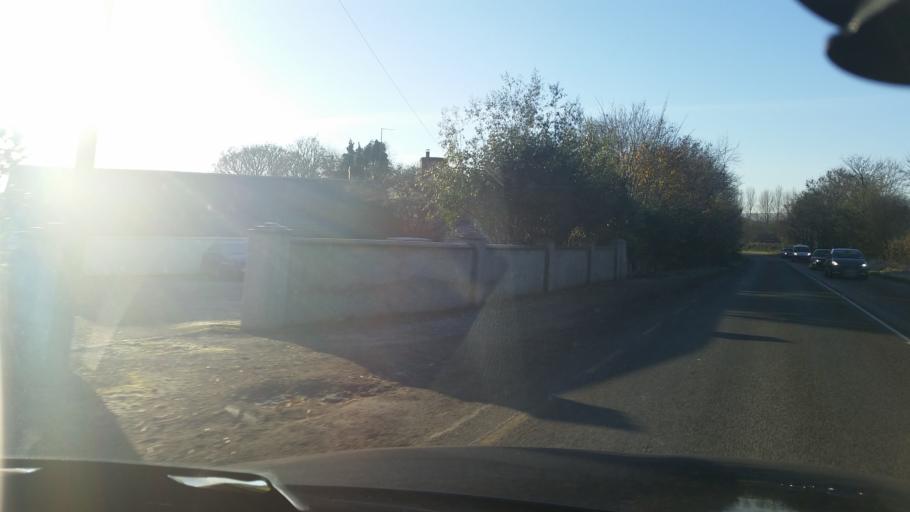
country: IE
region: Leinster
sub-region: Loch Garman
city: Gorey
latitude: 52.6331
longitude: -6.3046
